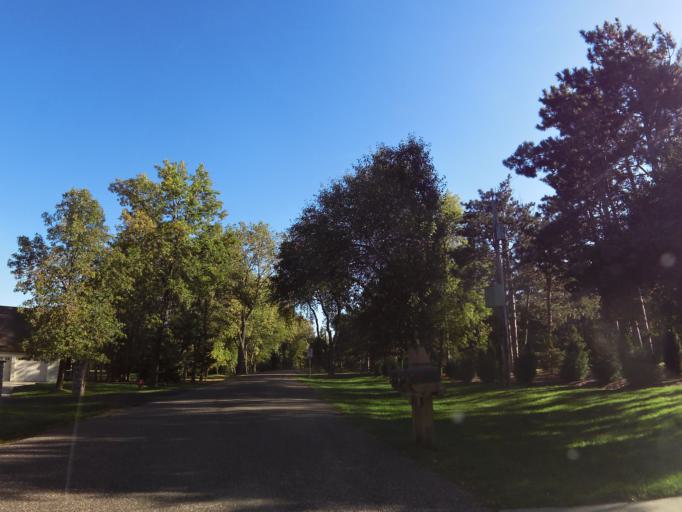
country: US
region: Minnesota
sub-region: Washington County
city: Lakeland
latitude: 44.9512
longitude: -92.7416
